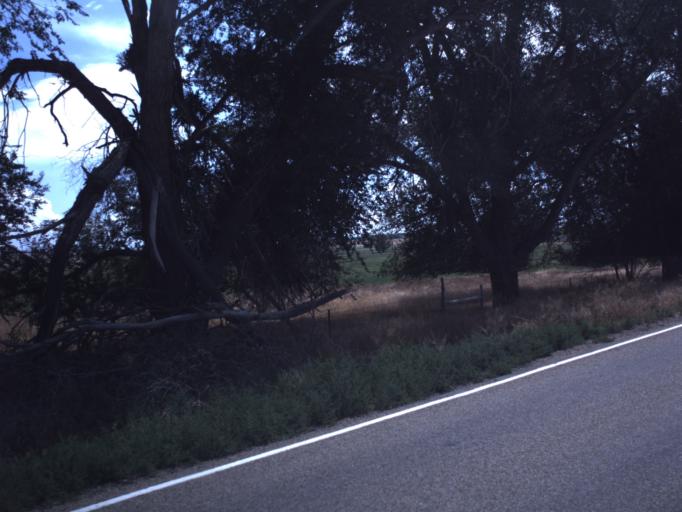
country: US
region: Utah
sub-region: Uintah County
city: Maeser
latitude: 40.2520
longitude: -109.6844
